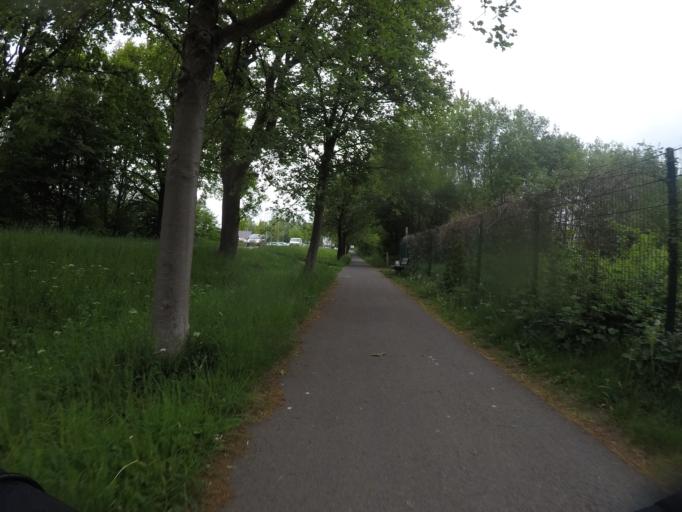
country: DE
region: Schleswig-Holstein
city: Kisdorf
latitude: 53.8005
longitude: 10.0045
